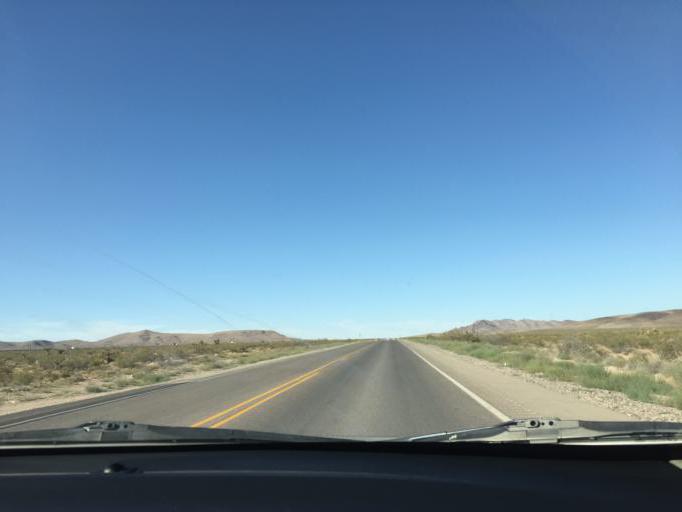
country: US
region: Nevada
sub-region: Clark County
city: Enterprise
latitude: 35.8428
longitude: -115.2685
